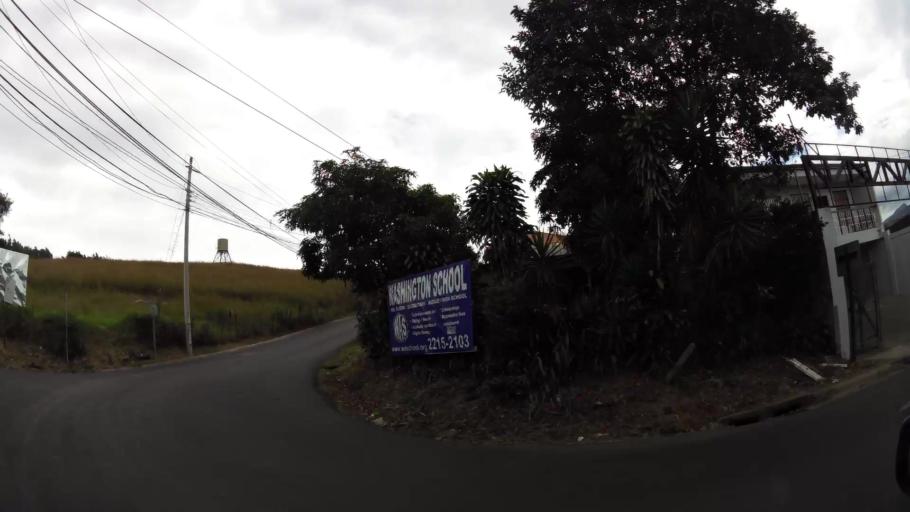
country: CR
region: Heredia
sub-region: Canton de Belen
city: San Antonio
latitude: 9.9610
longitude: -84.1910
